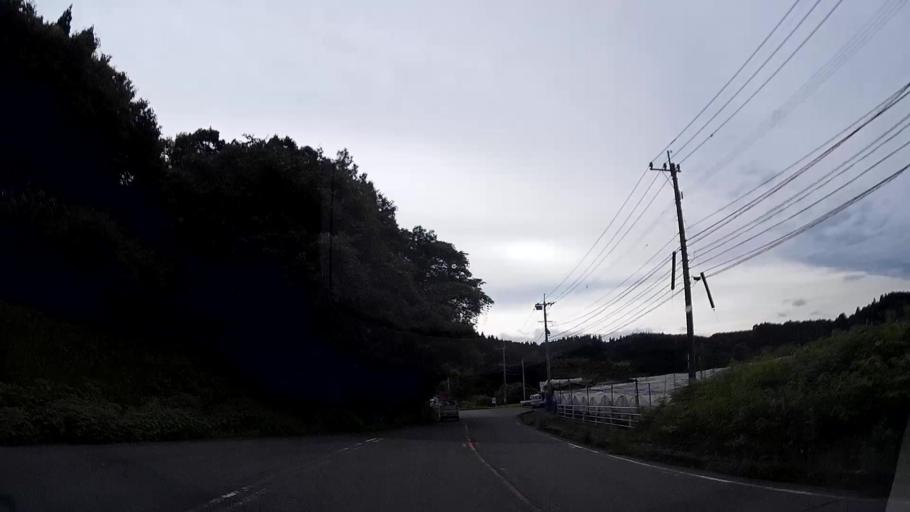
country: JP
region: Kumamoto
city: Kikuchi
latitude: 33.0160
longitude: 130.8692
